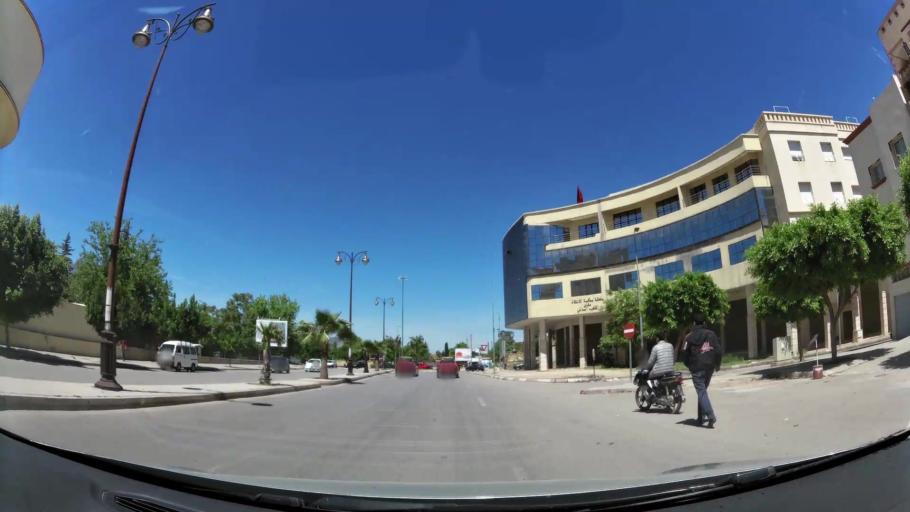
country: MA
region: Fes-Boulemane
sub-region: Fes
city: Fes
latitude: 34.0273
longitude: -5.0028
